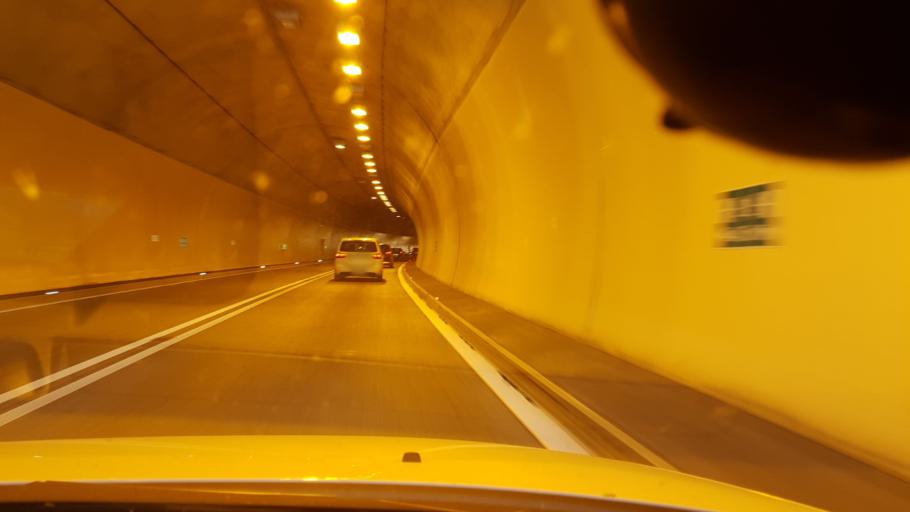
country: AT
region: Upper Austria
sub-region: Politischer Bezirk Kirchdorf an der Krems
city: Micheldorf in Oberoesterreich
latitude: 47.8165
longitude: 14.1702
